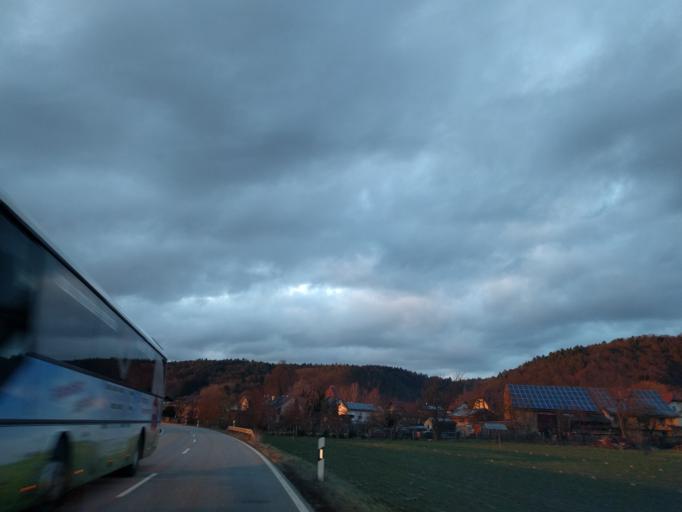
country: DE
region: Bavaria
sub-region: Lower Bavaria
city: Winzer
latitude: 48.7122
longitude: 13.1047
